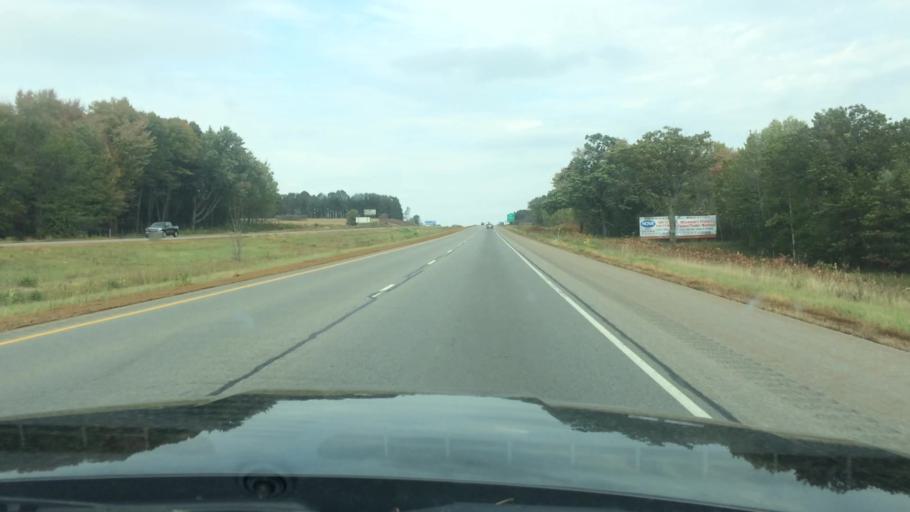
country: US
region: Wisconsin
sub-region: Marathon County
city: Mosinee
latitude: 44.7625
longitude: -89.6799
